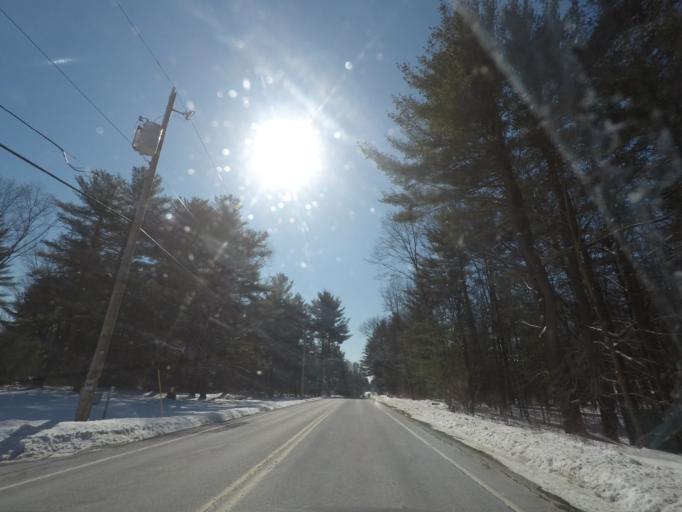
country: US
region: New York
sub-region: Saratoga County
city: Country Knolls
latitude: 42.9239
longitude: -73.8231
